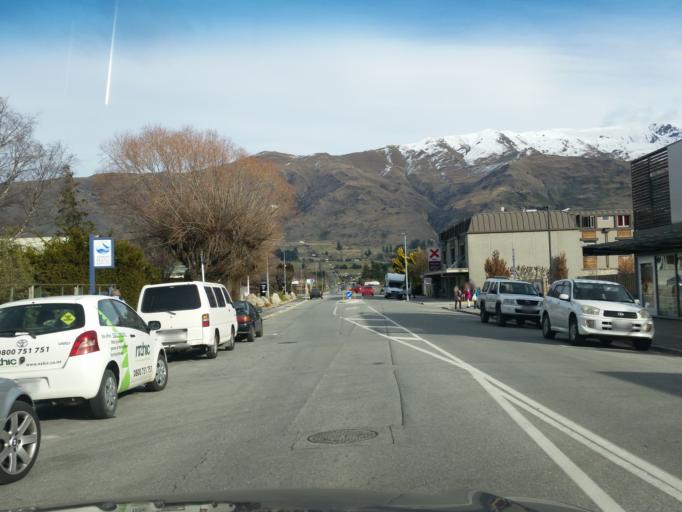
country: NZ
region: Otago
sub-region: Queenstown-Lakes District
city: Wanaka
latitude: -44.6968
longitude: 169.1362
